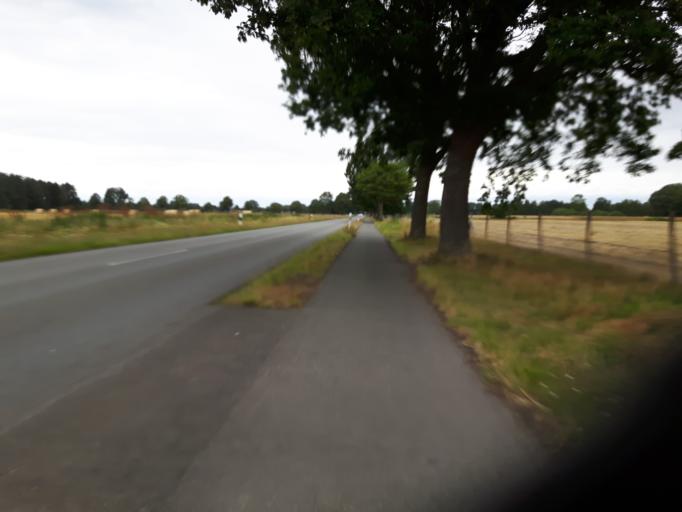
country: DE
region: Lower Saxony
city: Stuhr
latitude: 53.0066
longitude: 8.7718
